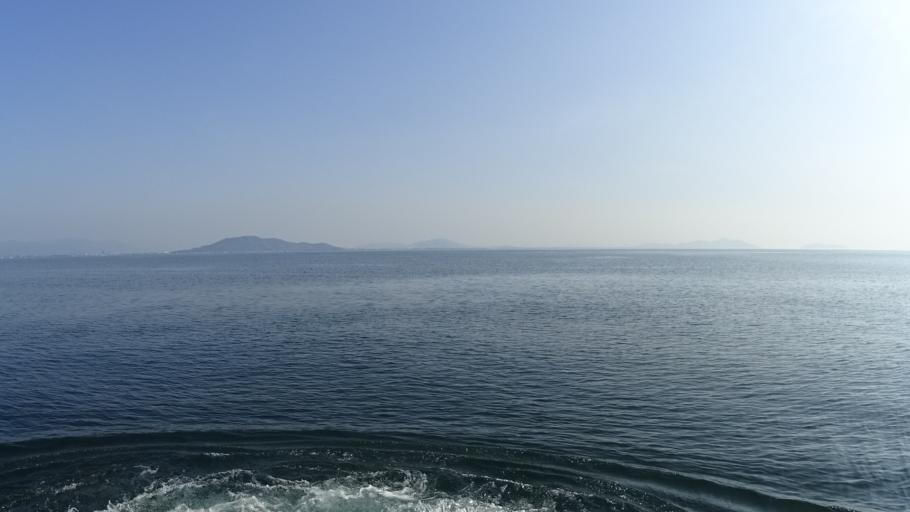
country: JP
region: Shiga Prefecture
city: Hikone
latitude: 35.2958
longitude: 136.1790
